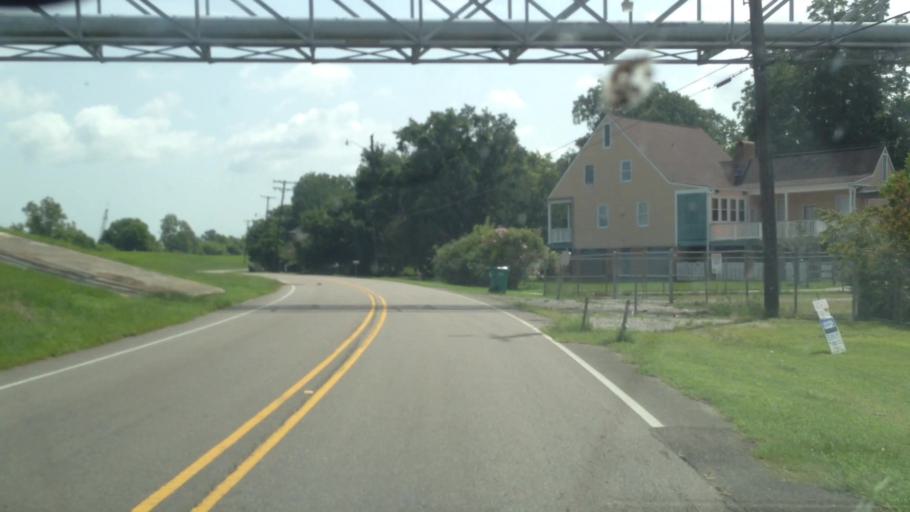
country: US
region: Louisiana
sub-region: Jefferson Parish
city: Jefferson
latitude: 29.9492
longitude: -90.1557
